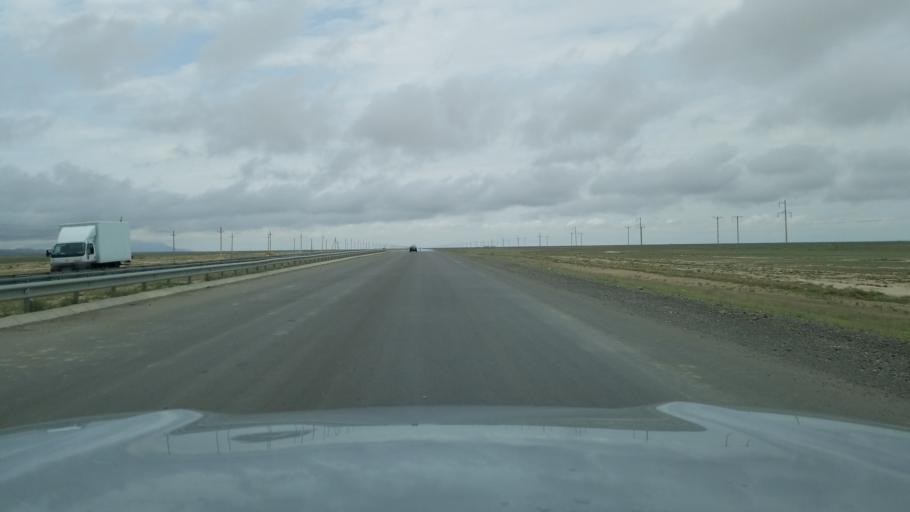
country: TM
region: Balkan
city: Gazanjyk
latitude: 39.1273
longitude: 55.8958
